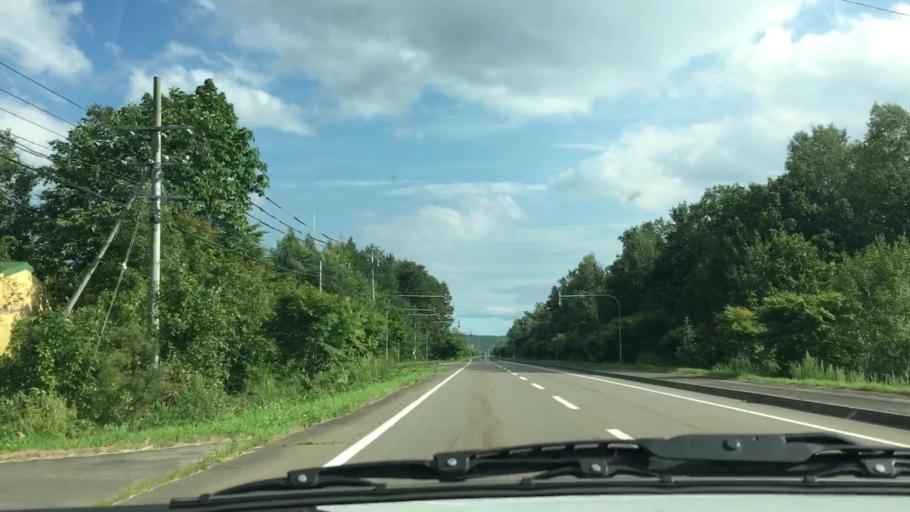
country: JP
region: Hokkaido
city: Otofuke
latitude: 43.3190
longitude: 143.3032
